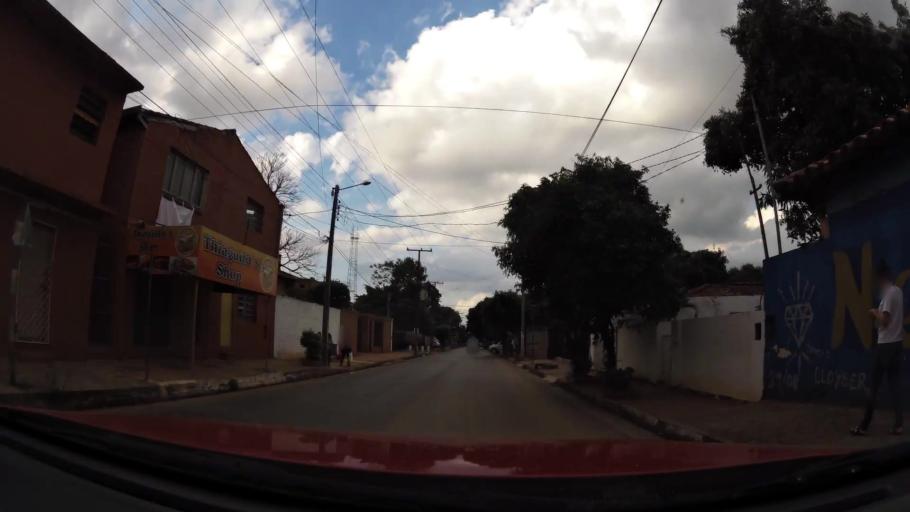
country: PY
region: Central
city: Fernando de la Mora
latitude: -25.3371
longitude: -57.5449
